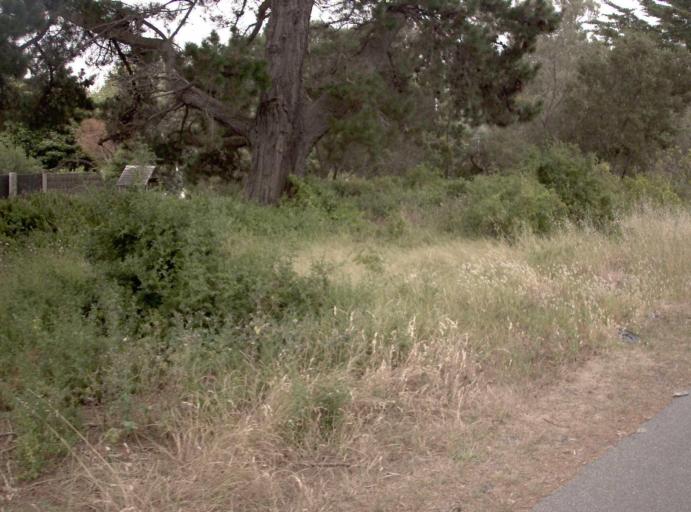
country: AU
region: Victoria
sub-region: Mornington Peninsula
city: Sorrento
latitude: -38.3313
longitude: 144.7378
